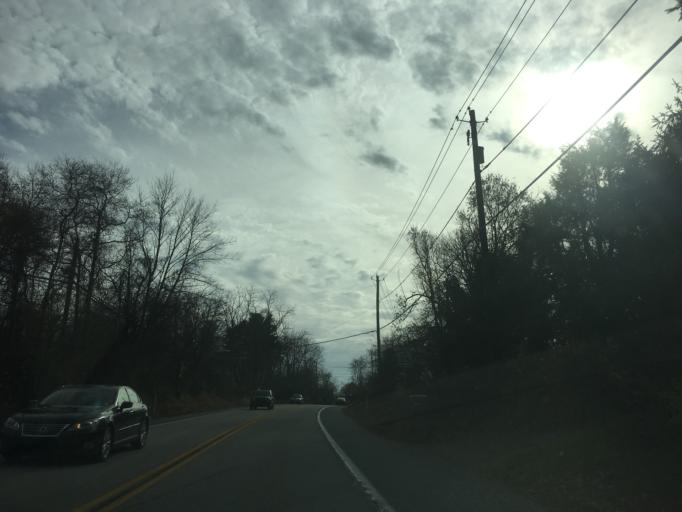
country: US
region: Pennsylvania
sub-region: Dauphin County
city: Colonial Park
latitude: 40.3160
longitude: -76.8224
